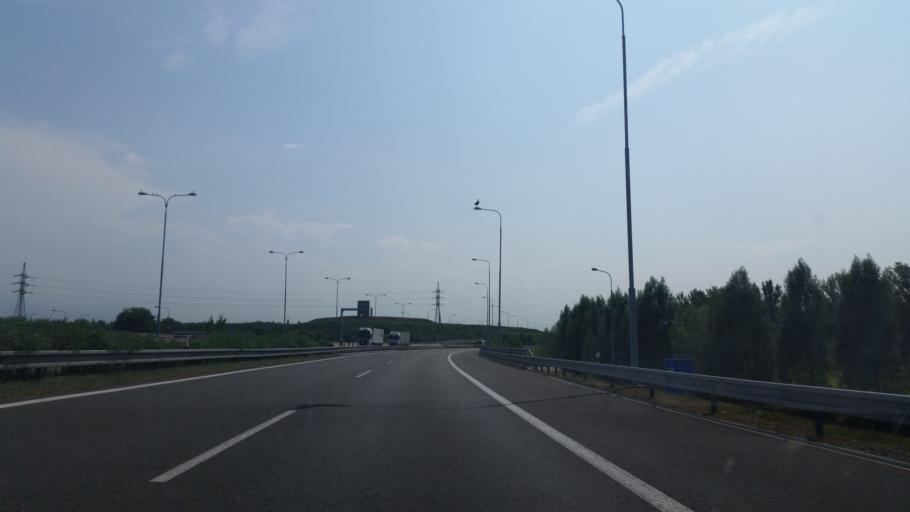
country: PL
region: Silesian Voivodeship
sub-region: Powiat raciborski
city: Chalupki
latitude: 49.8812
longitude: 18.3055
